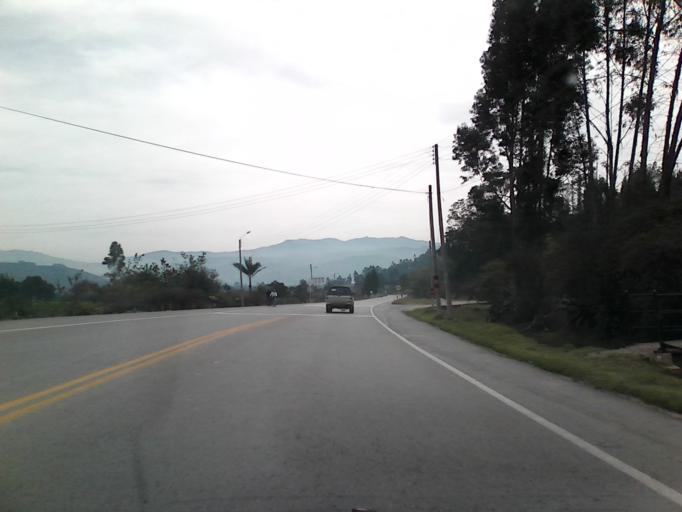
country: CO
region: Boyaca
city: Tibasosa
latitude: 5.7459
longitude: -72.9924
